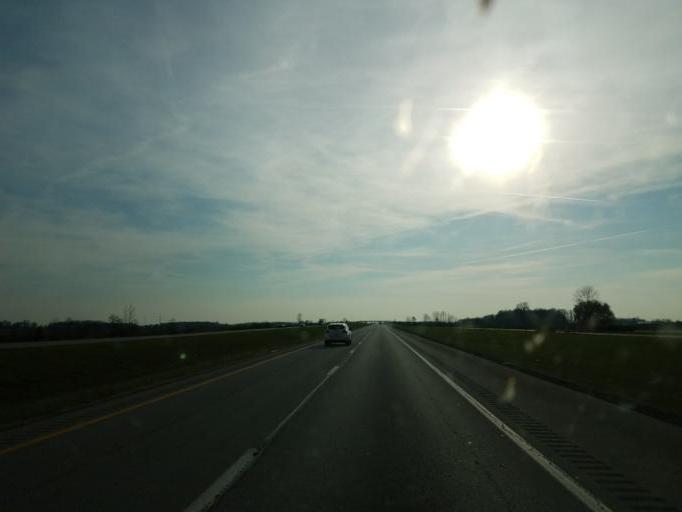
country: US
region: Ohio
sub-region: Clinton County
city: Wilmington
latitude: 39.5336
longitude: -83.7939
